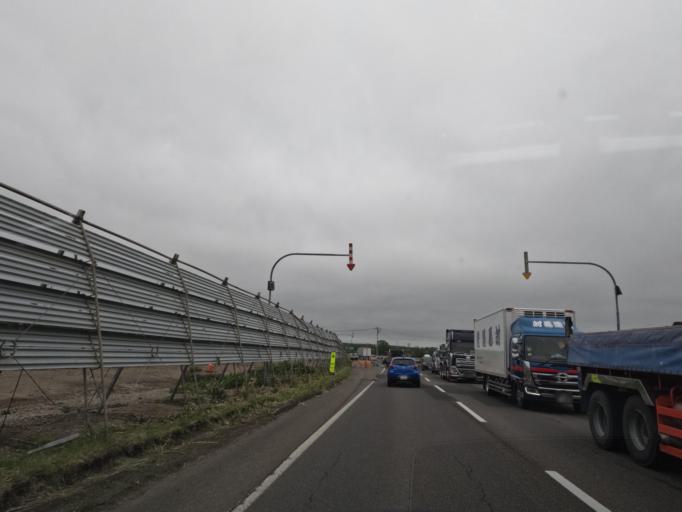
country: JP
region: Hokkaido
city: Ebetsu
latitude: 43.1401
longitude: 141.5150
